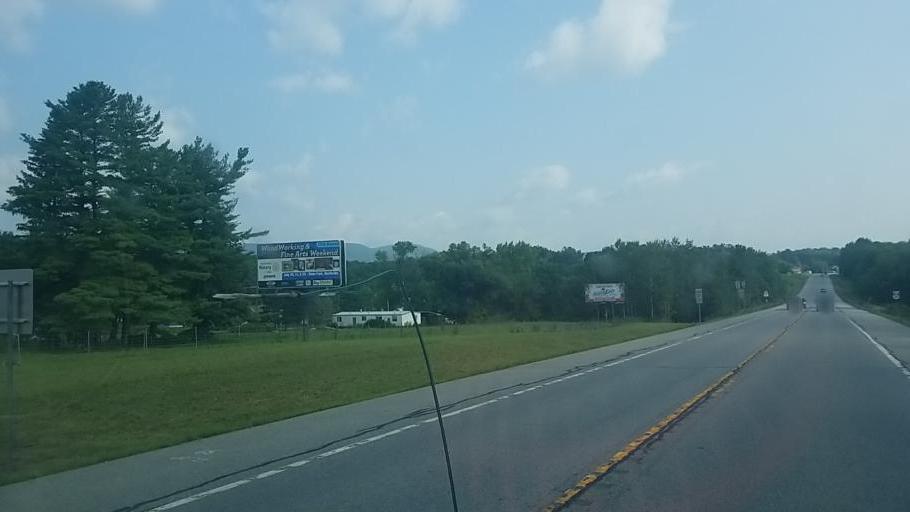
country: US
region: New York
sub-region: Fulton County
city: Gloversville
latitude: 43.0954
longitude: -74.2787
